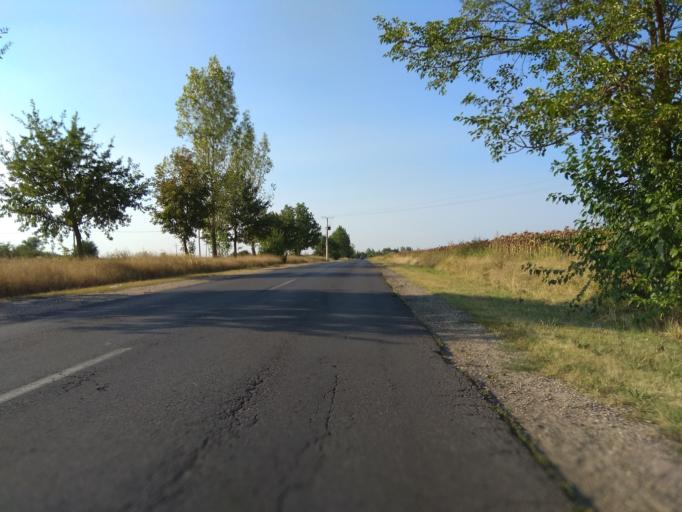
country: HU
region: Borsod-Abauj-Zemplen
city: Onod
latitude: 47.9889
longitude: 20.9238
